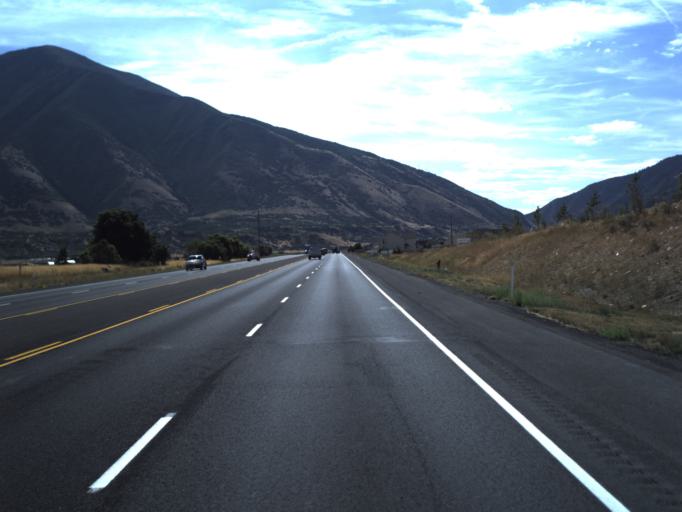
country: US
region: Utah
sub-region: Utah County
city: Mapleton
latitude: 40.0981
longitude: -111.6103
